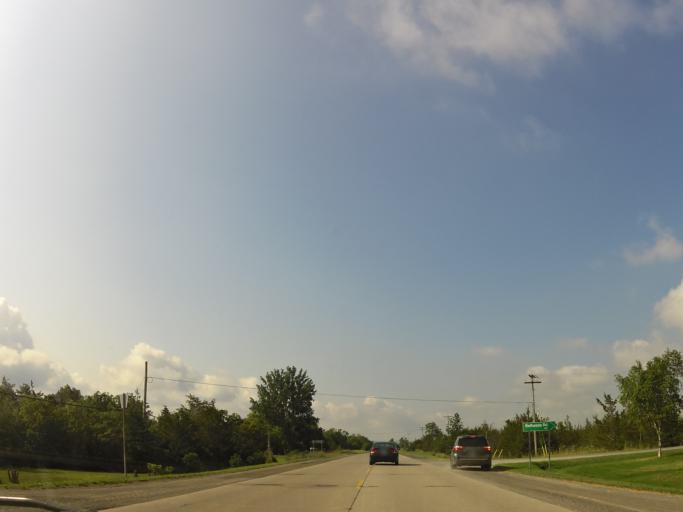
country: CA
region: Ontario
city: Picton
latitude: 44.0822
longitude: -77.0931
